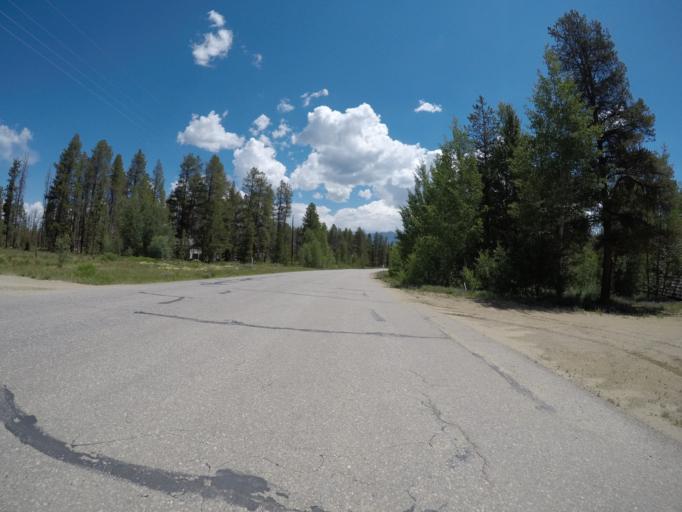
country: US
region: Colorado
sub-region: Grand County
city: Fraser
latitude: 39.9504
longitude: -105.8347
